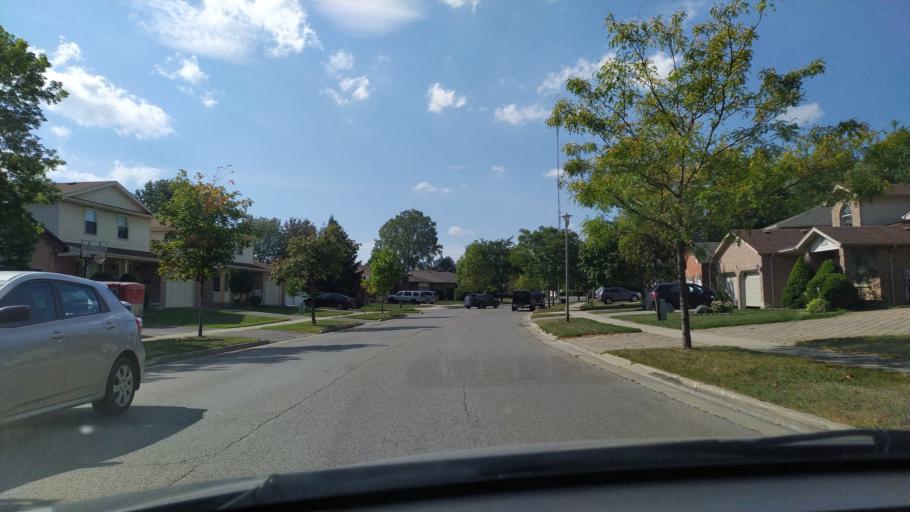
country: CA
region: Ontario
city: London
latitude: 42.9470
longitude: -81.2532
